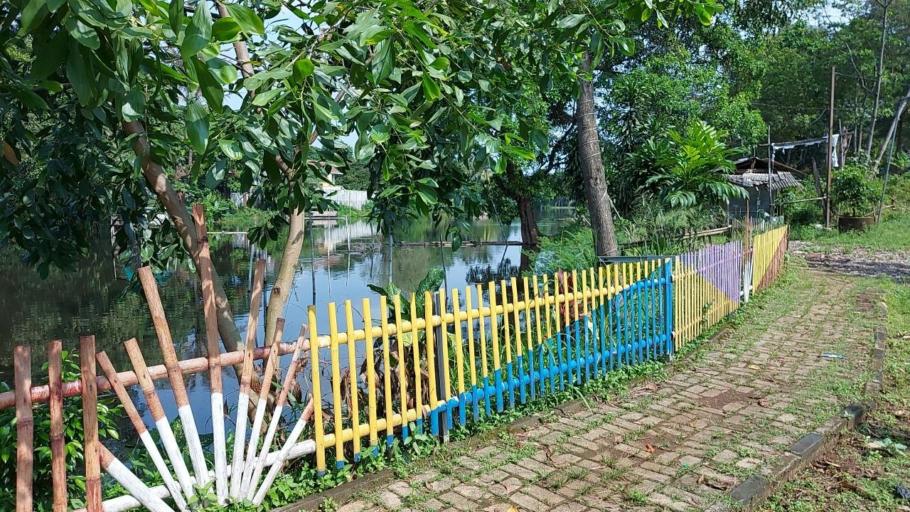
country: ID
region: West Java
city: Cibinong
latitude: -6.4718
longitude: 106.8373
